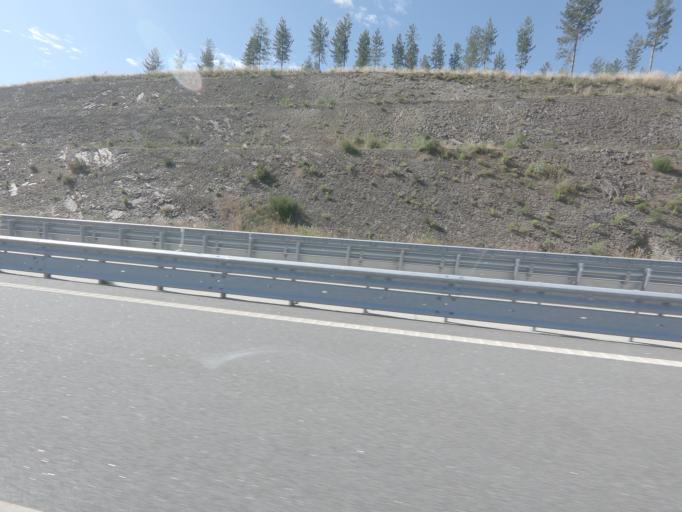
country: PT
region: Vila Real
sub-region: Santa Marta de Penaguiao
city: Santa Marta de Penaguiao
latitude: 41.2797
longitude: -7.8408
